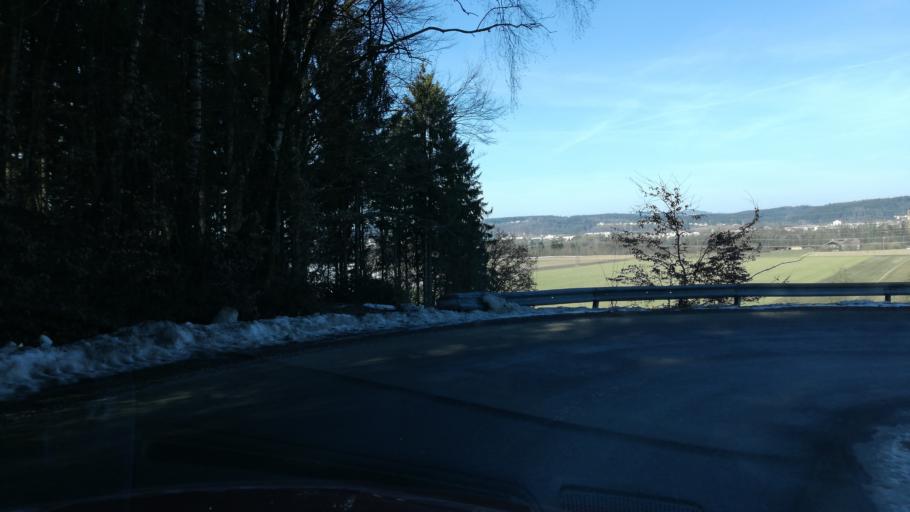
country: AT
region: Upper Austria
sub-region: Politischer Bezirk Vocklabruck
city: Vocklabruck
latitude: 47.9867
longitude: 13.6545
